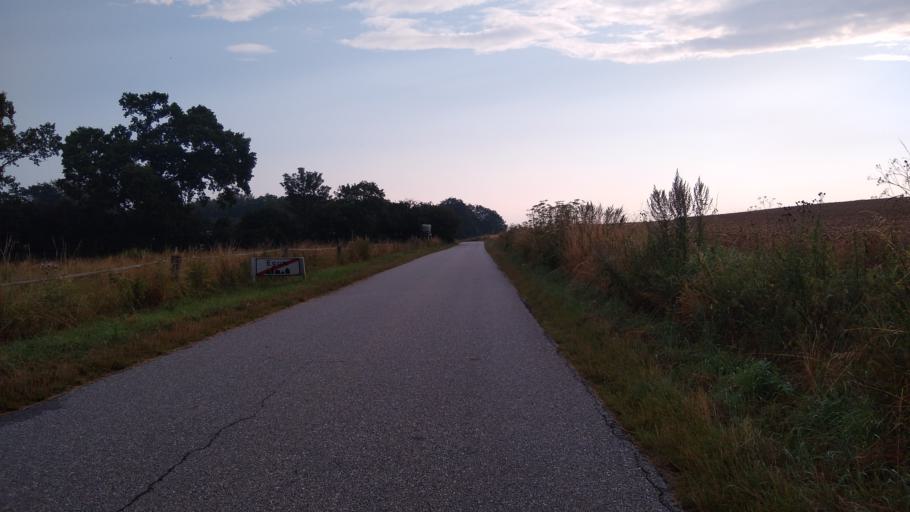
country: DK
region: South Denmark
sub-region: Fredericia Kommune
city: Fredericia
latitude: 55.5975
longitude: 9.7101
